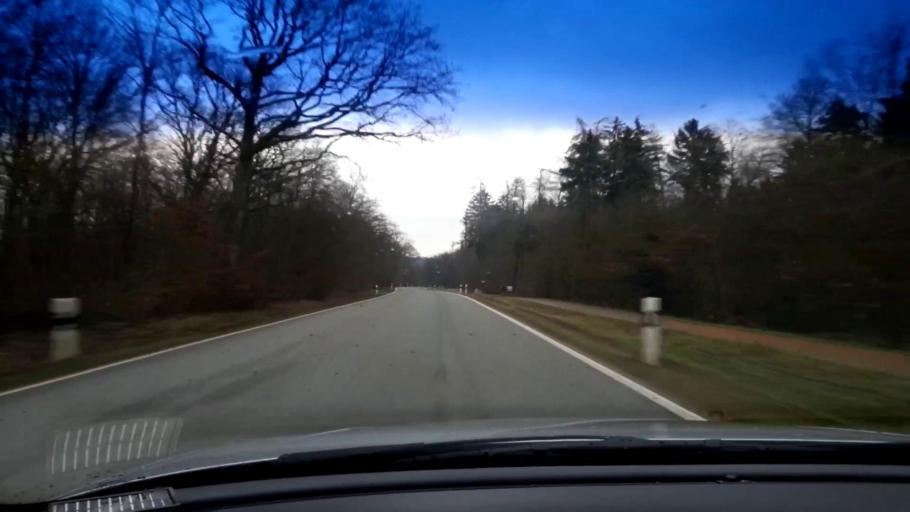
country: DE
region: Bavaria
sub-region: Upper Franconia
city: Litzendorf
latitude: 49.9308
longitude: 10.9913
